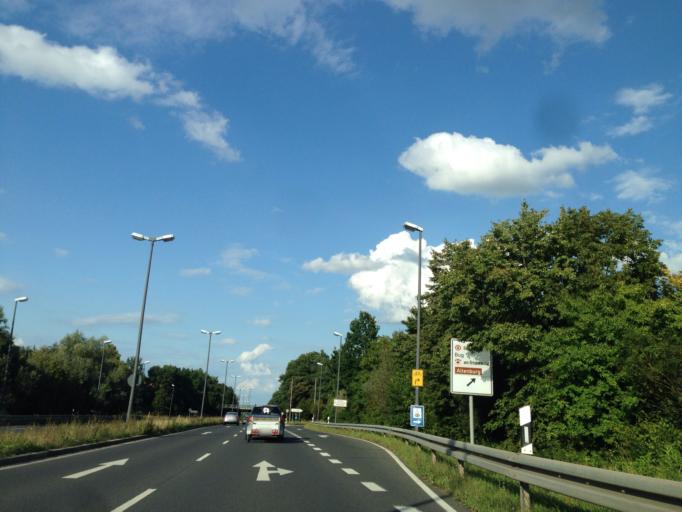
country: DE
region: Bavaria
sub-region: Upper Franconia
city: Bamberg
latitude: 49.8728
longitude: 10.8849
